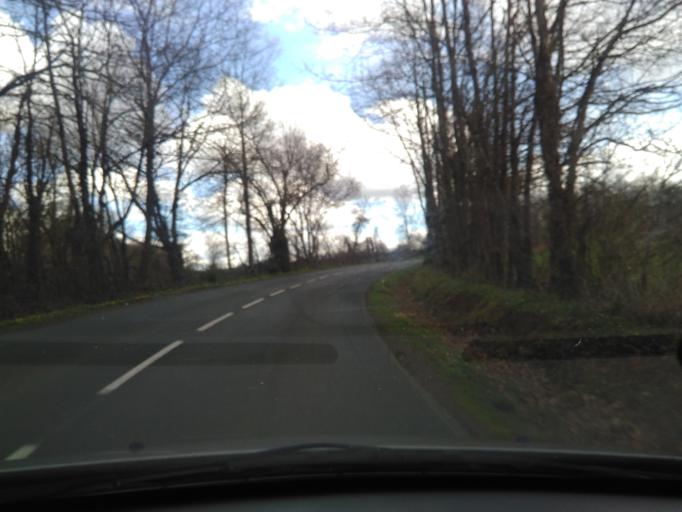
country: FR
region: Pays de la Loire
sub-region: Departement de la Vendee
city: Sainte-Cecile
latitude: 46.6909
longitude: -1.1143
